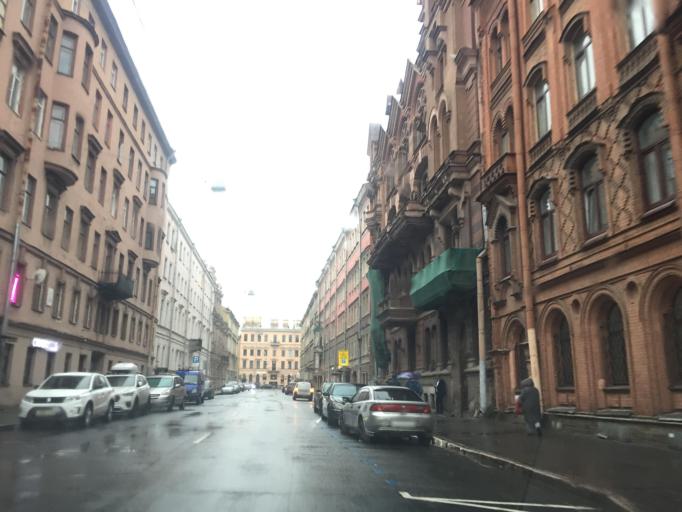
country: RU
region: St.-Petersburg
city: Centralniy
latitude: 59.9379
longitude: 30.3528
